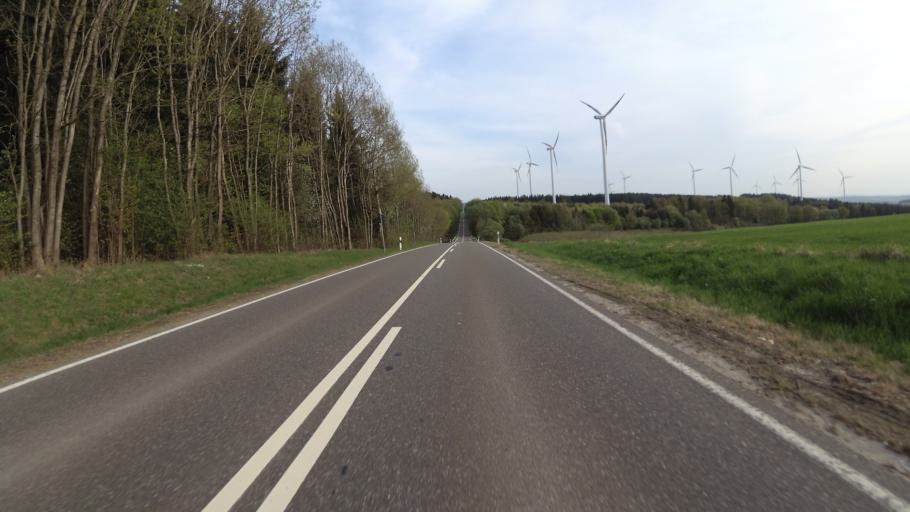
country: DE
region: Rheinland-Pfalz
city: Morbach
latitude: 49.8454
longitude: 7.1185
